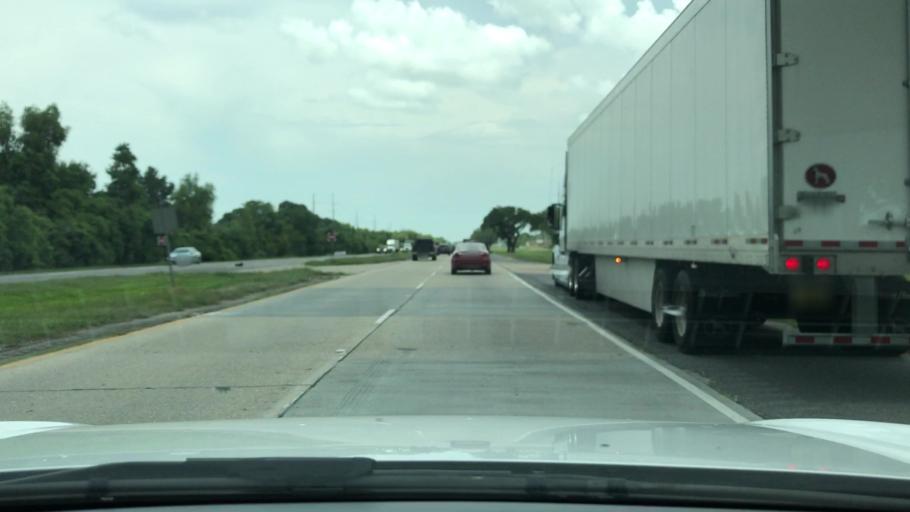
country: US
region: Louisiana
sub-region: Iberville Parish
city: Plaquemine
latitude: 30.3196
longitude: -91.2512
